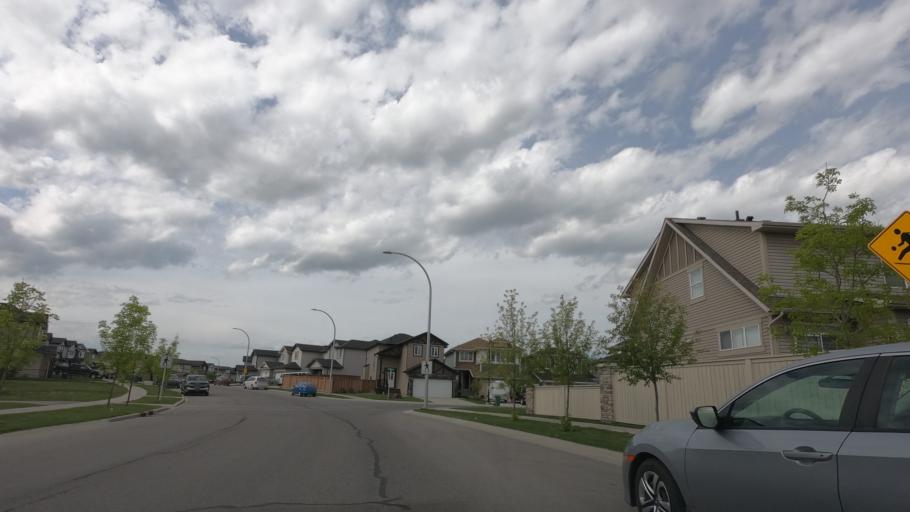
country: CA
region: Alberta
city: Airdrie
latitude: 51.2733
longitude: -114.0426
